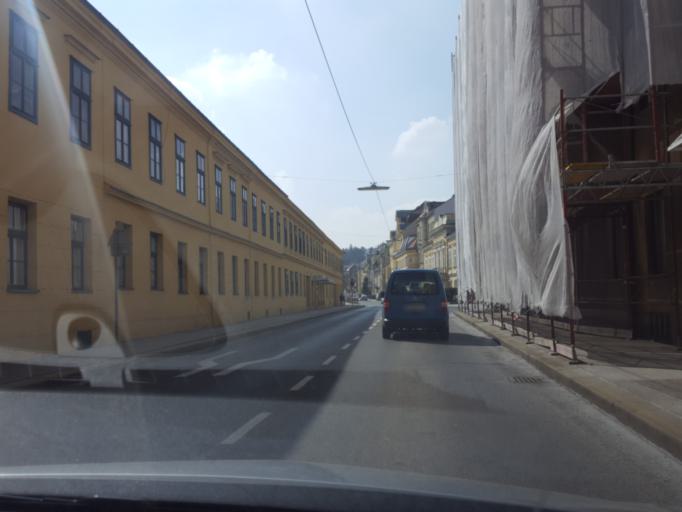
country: AT
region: Lower Austria
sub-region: Politischer Bezirk Modling
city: Perchtoldsdorf
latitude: 48.1847
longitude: 16.3006
